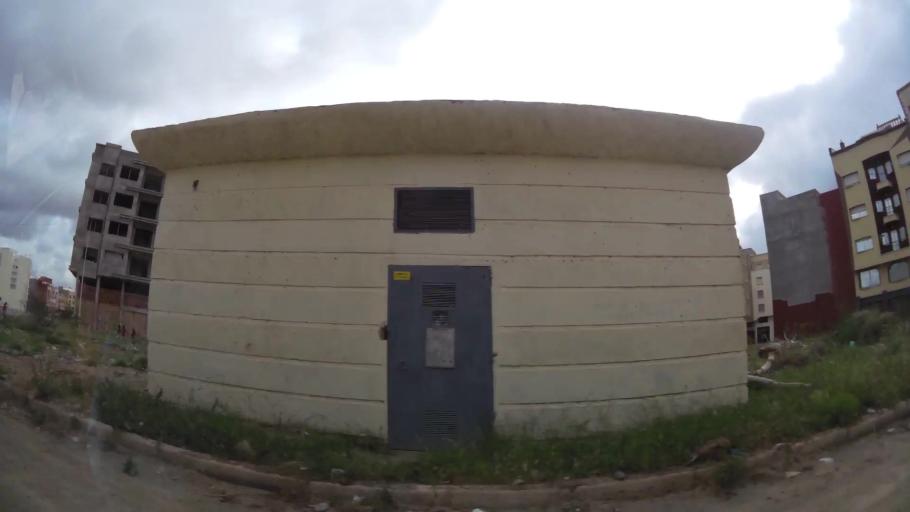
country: MA
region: Oriental
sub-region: Nador
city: Nador
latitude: 35.1535
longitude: -2.9248
